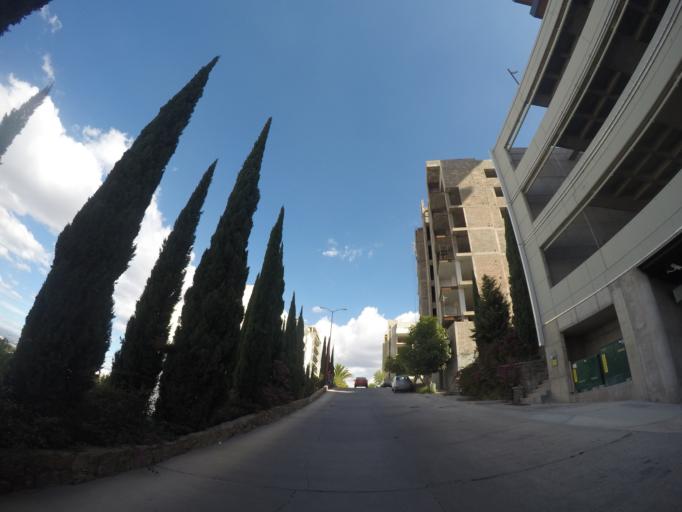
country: MX
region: San Luis Potosi
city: Escalerillas
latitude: 22.1226
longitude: -101.0337
